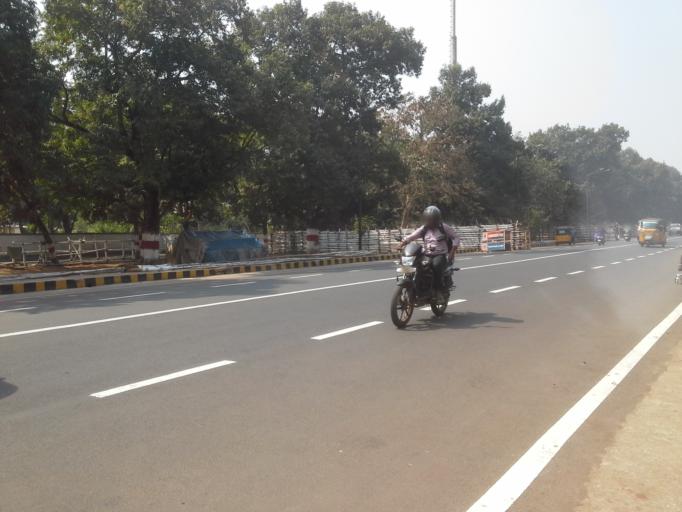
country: IN
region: Odisha
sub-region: Khordha
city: Bhubaneshwar
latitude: 20.2703
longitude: 85.8369
